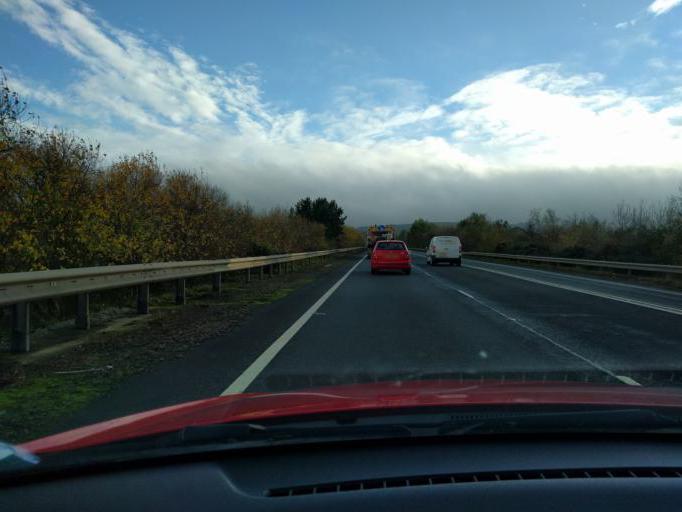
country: GB
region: Scotland
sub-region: The Scottish Borders
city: Duns
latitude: 55.9340
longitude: -2.3560
